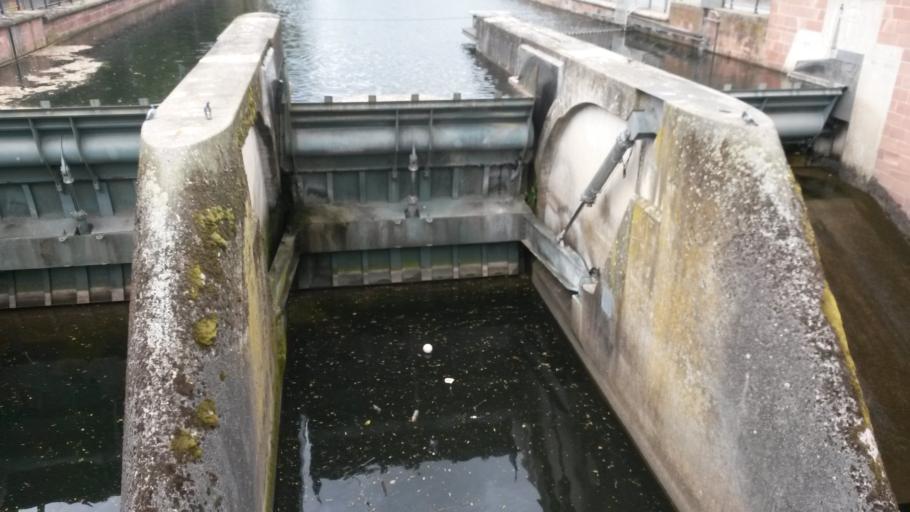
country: DE
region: Baden-Wuerttemberg
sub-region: Karlsruhe Region
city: Pforzheim
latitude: 48.8886
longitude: 8.7034
